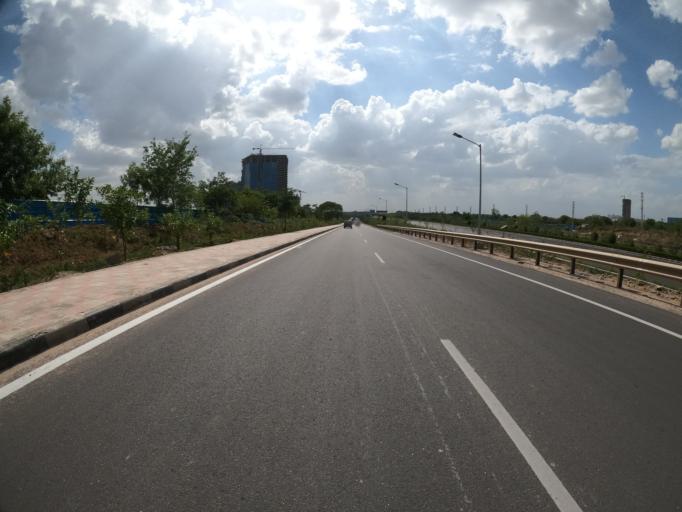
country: IN
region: Telangana
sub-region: Medak
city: Serilingampalle
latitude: 17.4032
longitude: 78.3372
